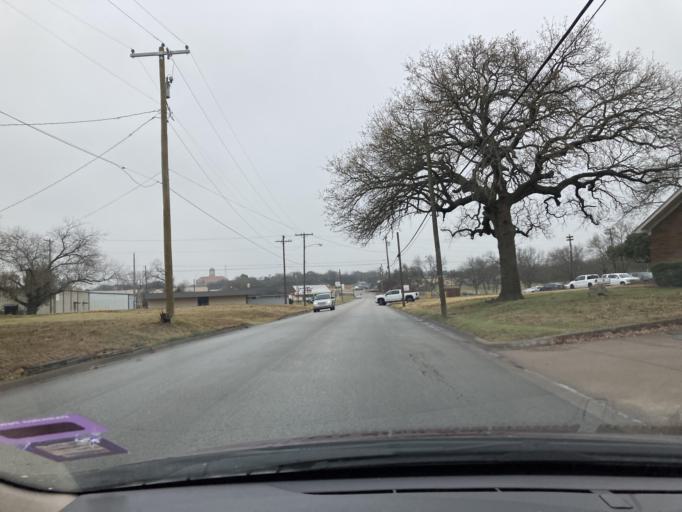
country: US
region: Texas
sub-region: Navarro County
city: Corsicana
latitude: 32.1027
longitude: -96.4730
